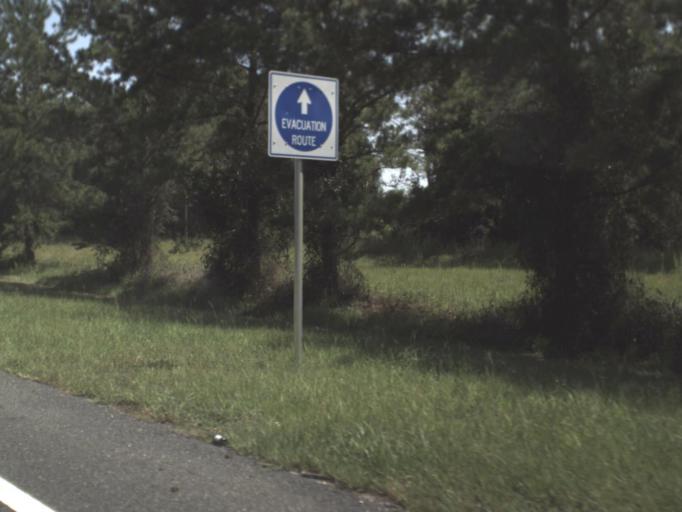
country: US
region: Florida
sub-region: Levy County
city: Chiefland
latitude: 29.4093
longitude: -82.8185
